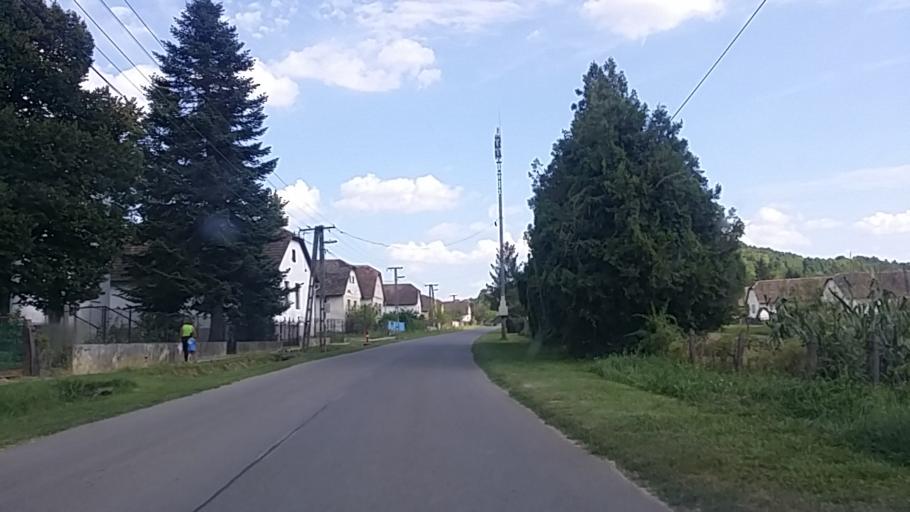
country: HU
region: Tolna
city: Gyonk
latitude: 46.5235
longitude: 18.5208
